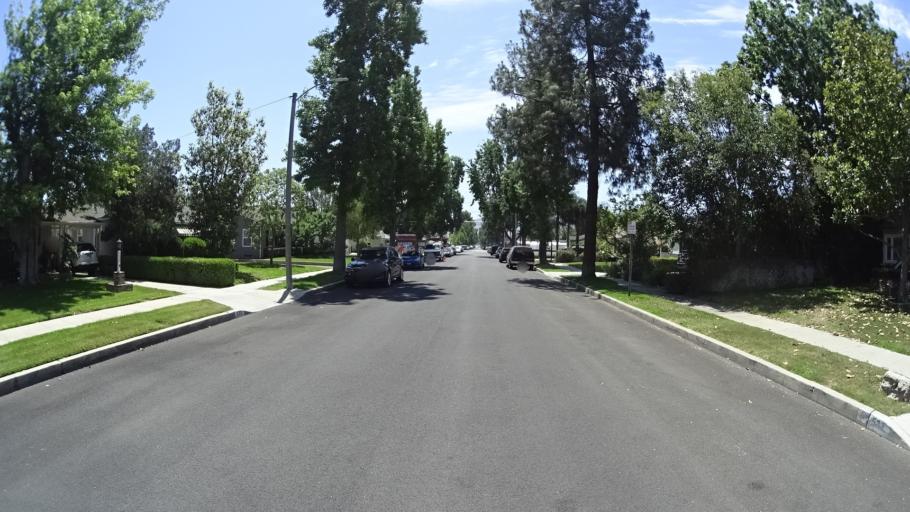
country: US
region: California
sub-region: Los Angeles County
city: Burbank
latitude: 34.1763
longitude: -118.3262
